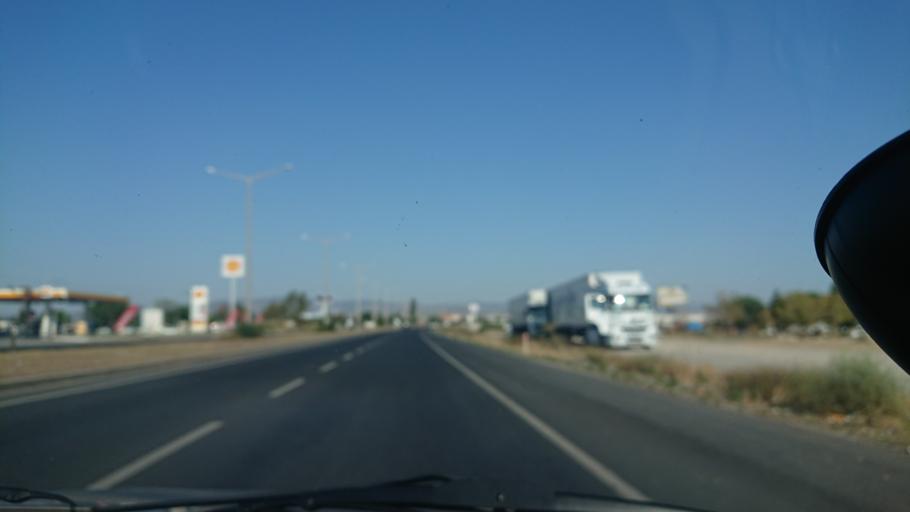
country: TR
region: Manisa
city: Adala
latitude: 38.5080
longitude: 28.2402
